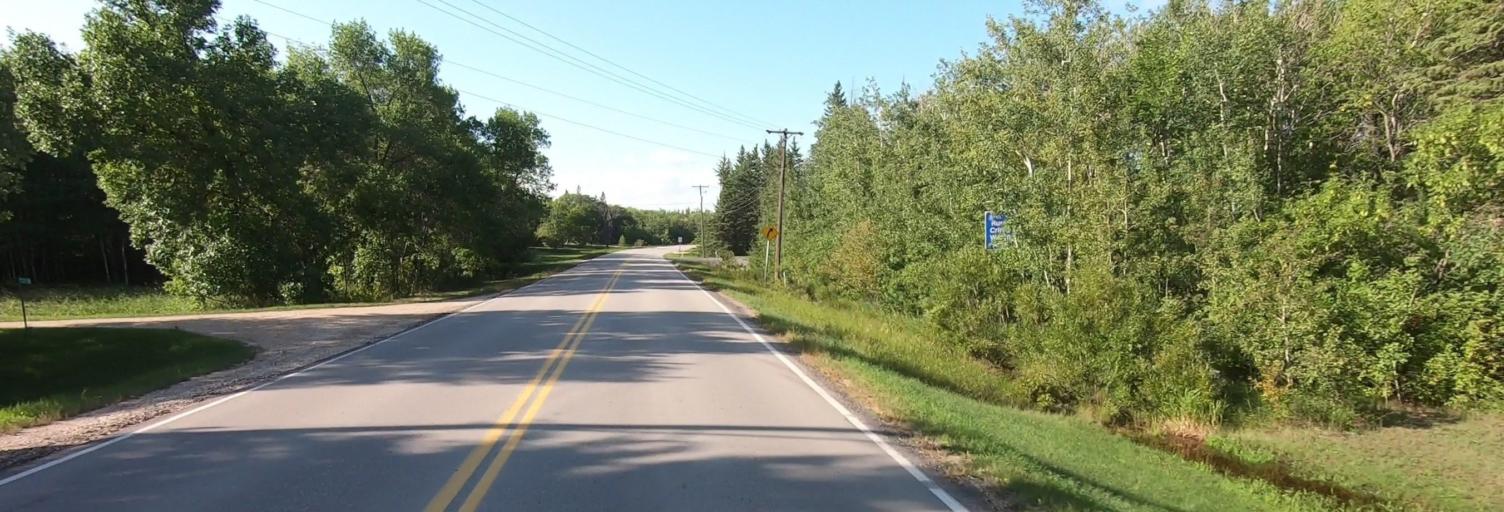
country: CA
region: Manitoba
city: Selkirk
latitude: 50.0944
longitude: -96.9323
